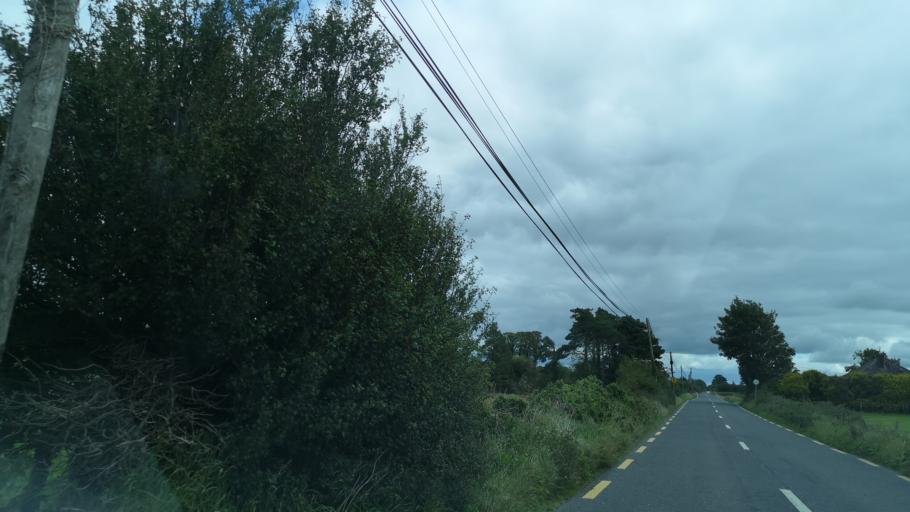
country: IE
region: Connaught
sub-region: County Galway
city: Ballinasloe
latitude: 53.3130
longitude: -8.1643
